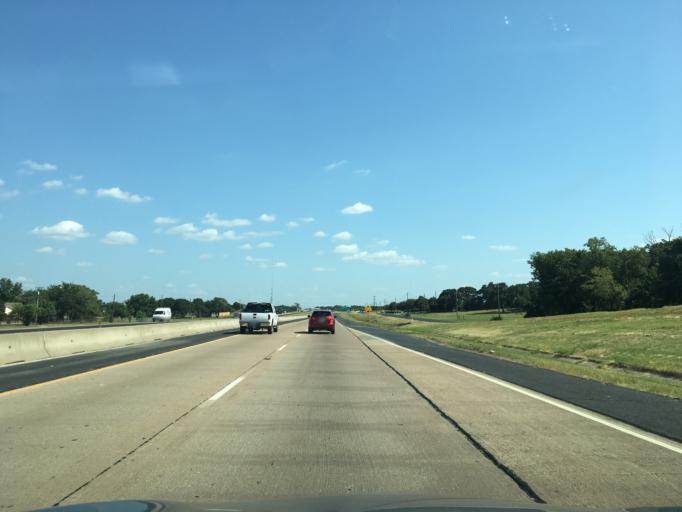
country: US
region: Texas
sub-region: Tarrant County
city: Kennedale
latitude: 32.6412
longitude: -97.1820
